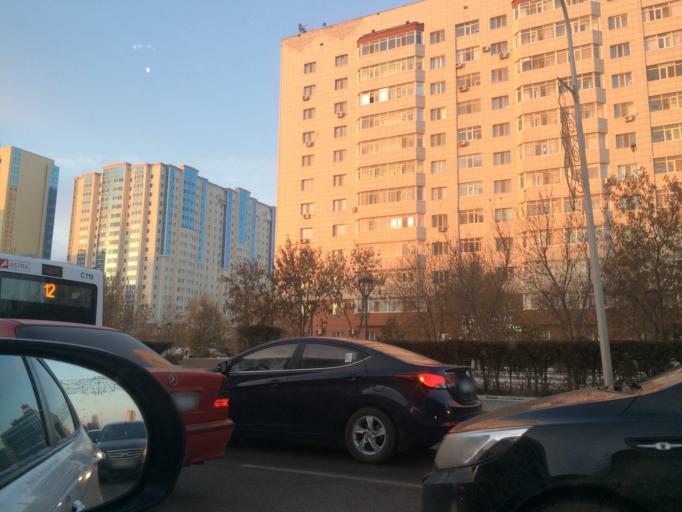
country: KZ
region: Astana Qalasy
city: Astana
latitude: 51.1640
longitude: 71.4095
